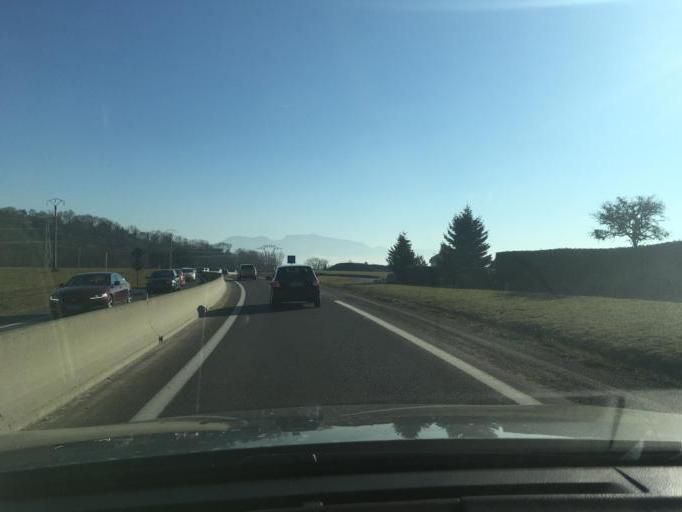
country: FR
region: Rhone-Alpes
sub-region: Departement de la Haute-Savoie
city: Cranves-Sales
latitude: 46.2030
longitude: 6.2912
